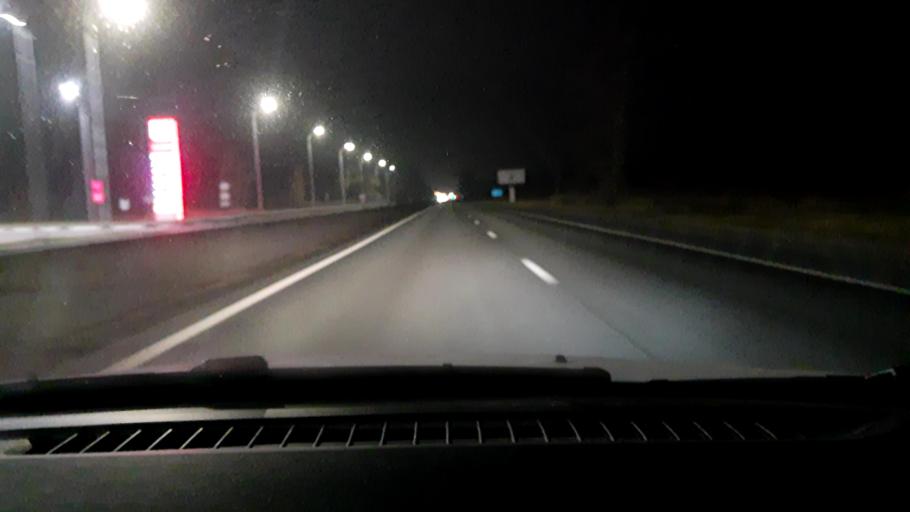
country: RU
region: Nizjnij Novgorod
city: Gorbatovka
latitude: 56.3103
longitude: 43.7891
